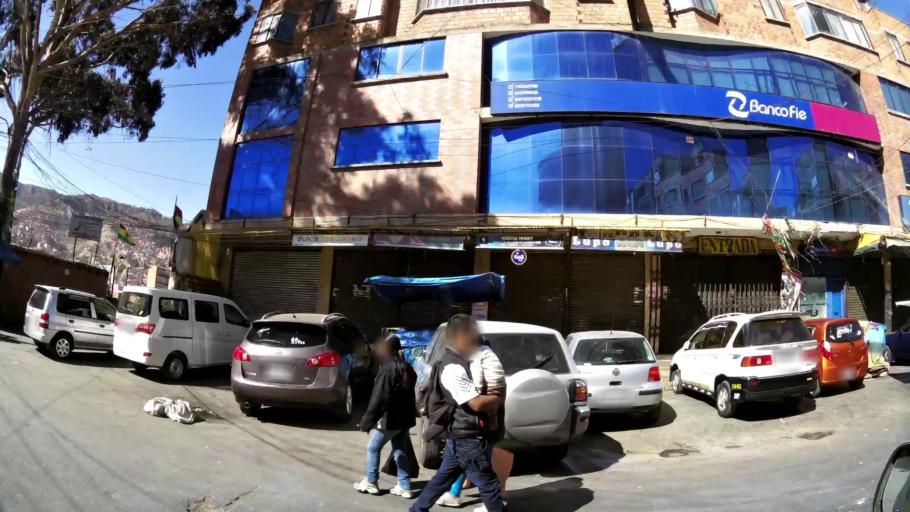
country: BO
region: La Paz
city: La Paz
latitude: -16.4938
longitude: -68.1441
